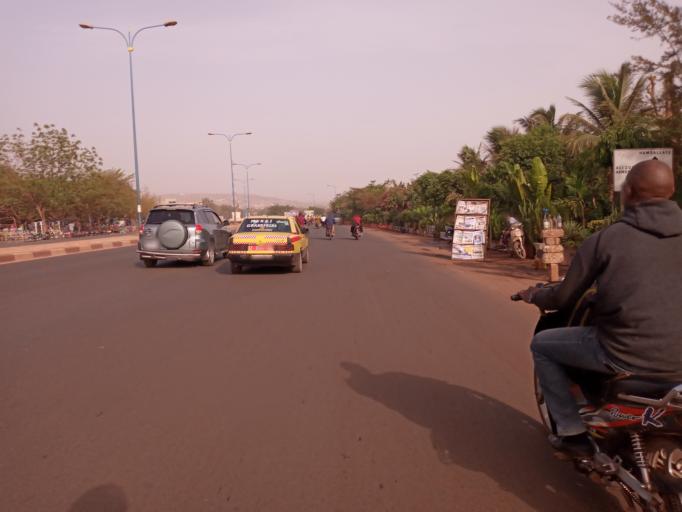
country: ML
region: Bamako
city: Bamako
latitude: 12.6359
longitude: -8.0151
